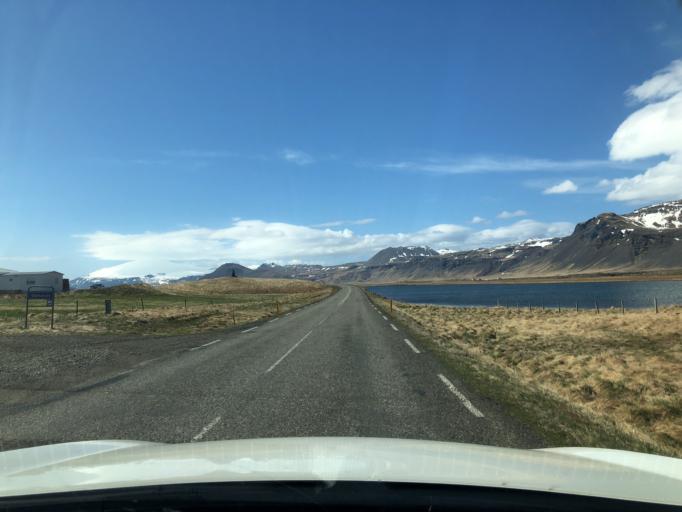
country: IS
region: West
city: Olafsvik
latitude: 64.8288
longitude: -23.2482
